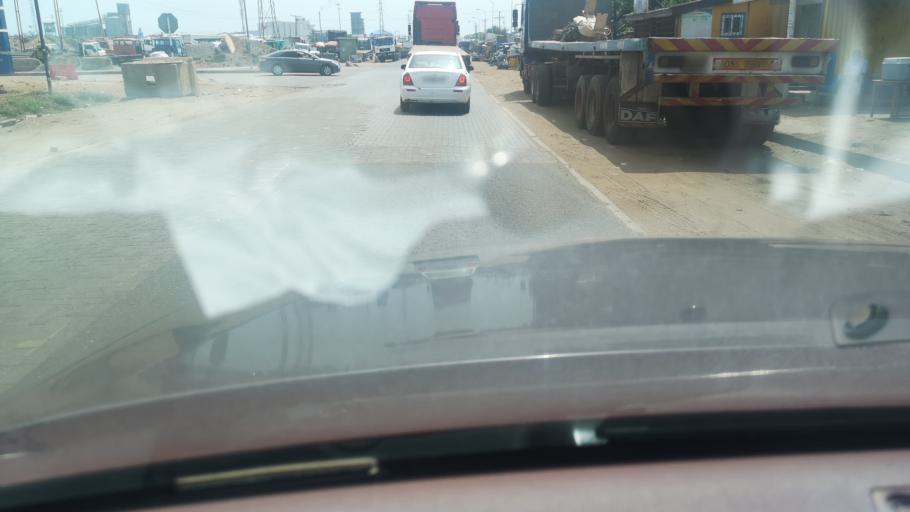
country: GH
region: Greater Accra
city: Tema
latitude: 5.6287
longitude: -0.0098
